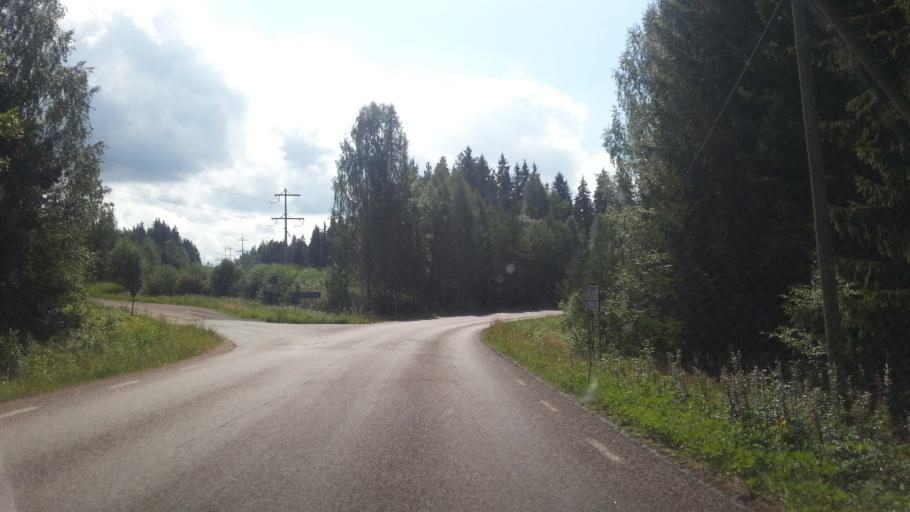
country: SE
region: Dalarna
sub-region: Faluns Kommun
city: Falun
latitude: 60.6447
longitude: 15.7854
